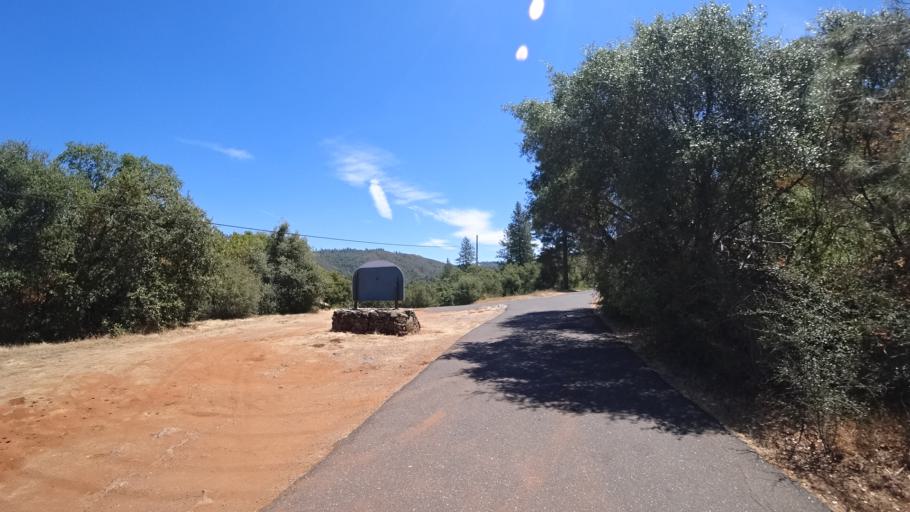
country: US
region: California
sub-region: Calaveras County
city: Murphys
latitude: 38.1511
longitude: -120.4773
